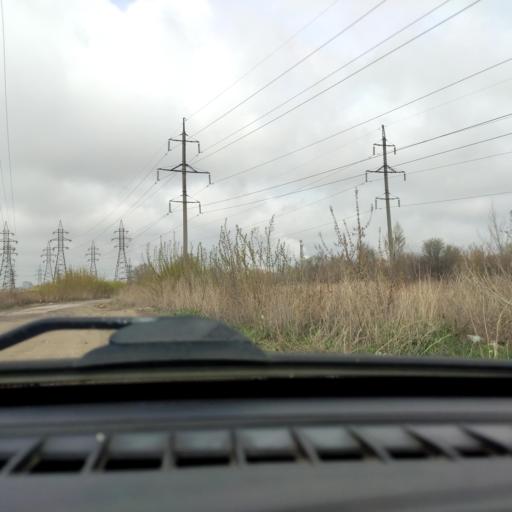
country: RU
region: Samara
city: Zhigulevsk
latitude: 53.5388
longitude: 49.4983
